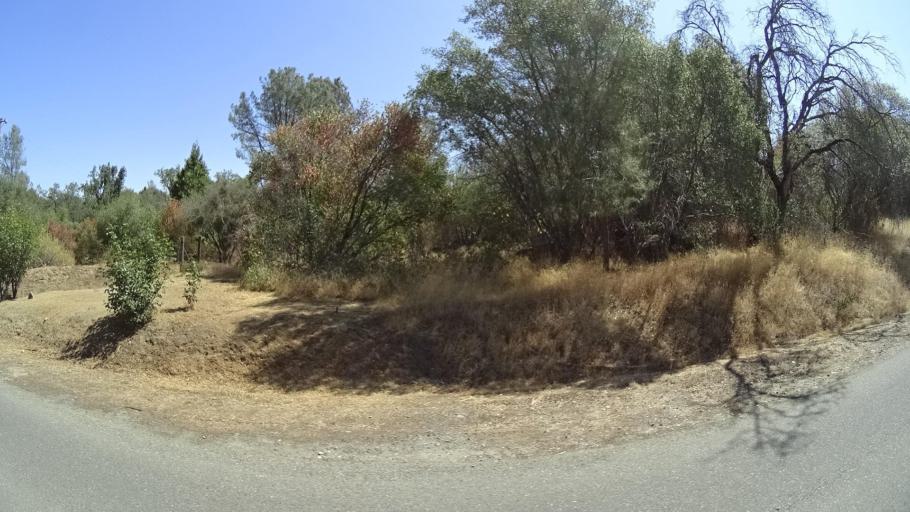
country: US
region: California
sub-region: Mariposa County
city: Mariposa
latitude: 37.4314
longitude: -119.9043
